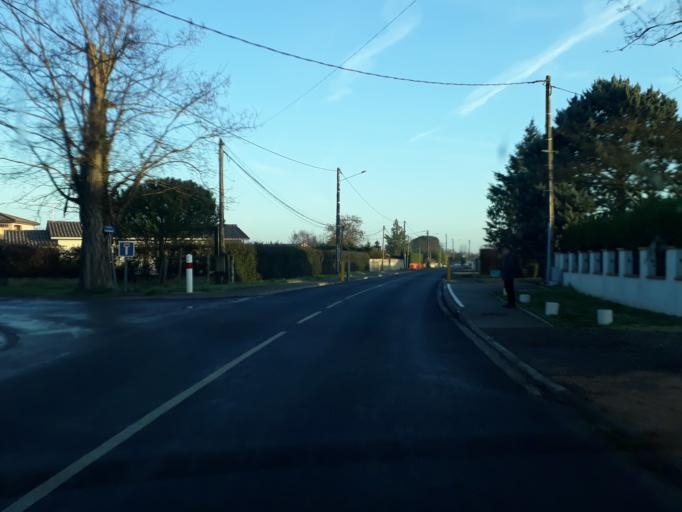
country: FR
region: Midi-Pyrenees
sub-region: Departement de la Haute-Garonne
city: Marquefave
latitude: 43.3226
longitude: 1.2294
